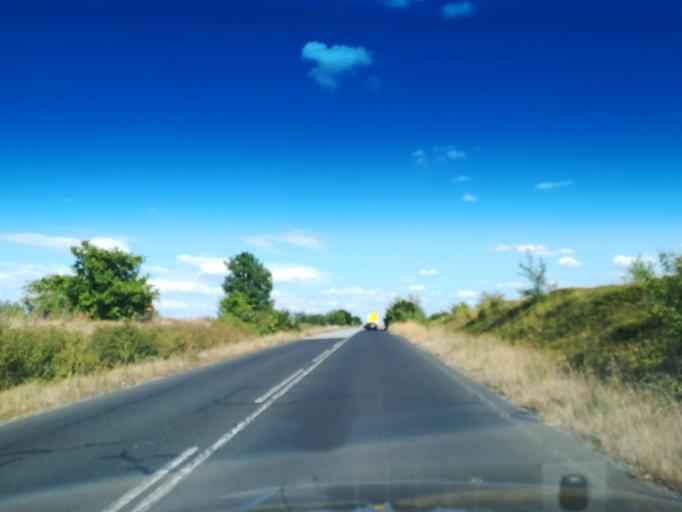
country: BG
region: Stara Zagora
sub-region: Obshtina Chirpan
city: Chirpan
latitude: 42.0590
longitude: 25.2764
